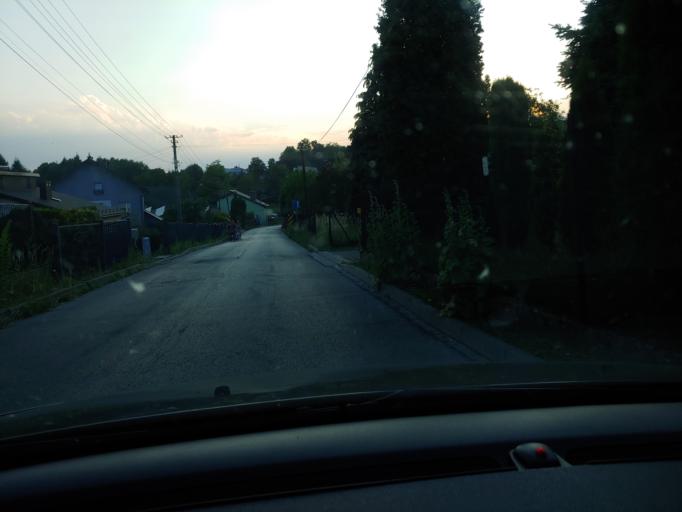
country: PL
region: Lesser Poland Voivodeship
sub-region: Powiat chrzanowski
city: Trzebinia
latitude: 50.1678
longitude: 19.4661
